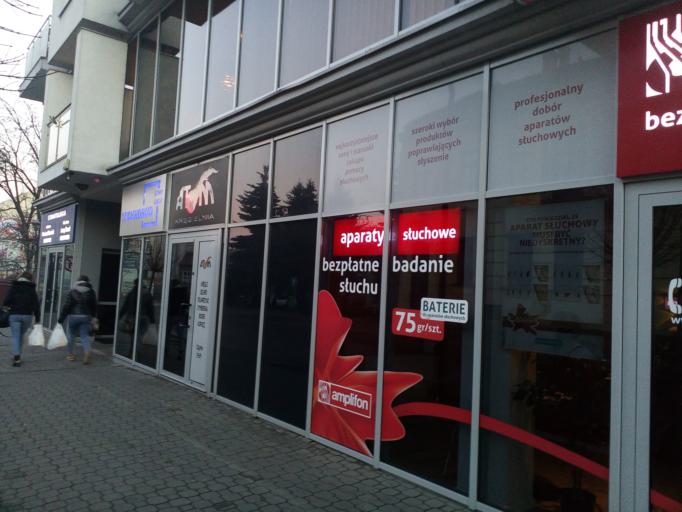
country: PL
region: Lesser Poland Voivodeship
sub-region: Powiat nowosadecki
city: Nowy Sacz
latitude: 49.6134
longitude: 20.6956
